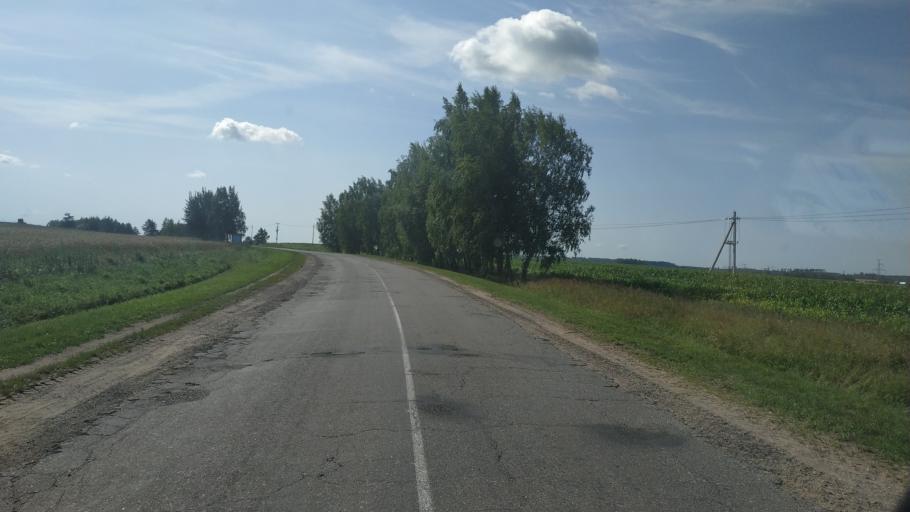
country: BY
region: Mogilev
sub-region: Mahilyowski Rayon
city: Veyno
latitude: 53.7859
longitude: 30.4342
